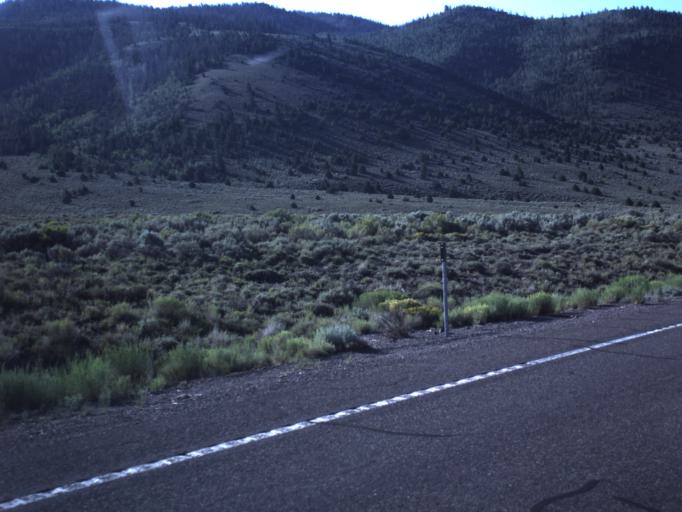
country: US
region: Utah
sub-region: Wayne County
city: Loa
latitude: 38.5394
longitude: -111.5121
